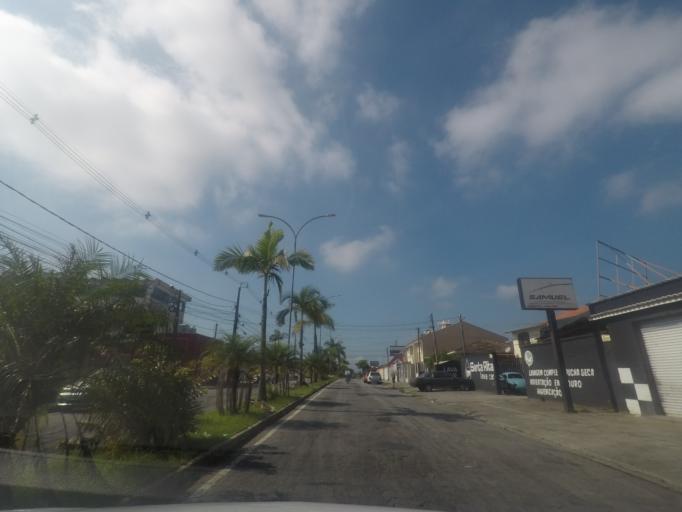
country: BR
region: Parana
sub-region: Paranagua
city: Paranagua
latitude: -25.5190
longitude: -48.5162
